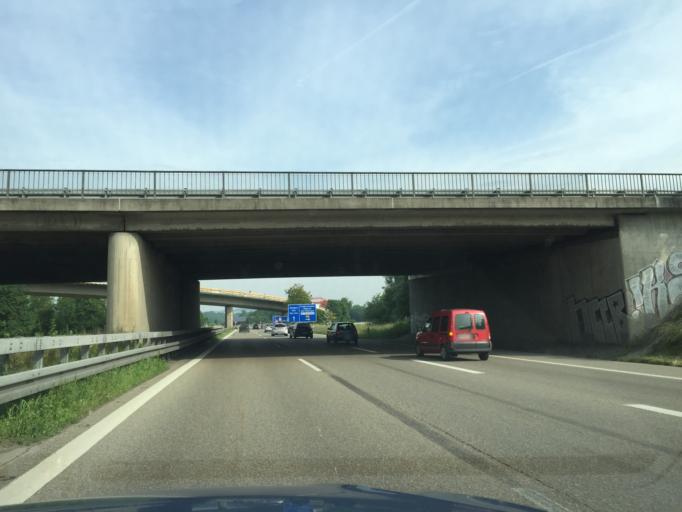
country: DE
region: Bavaria
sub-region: Swabia
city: Neu-Ulm
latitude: 48.3700
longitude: 9.9967
